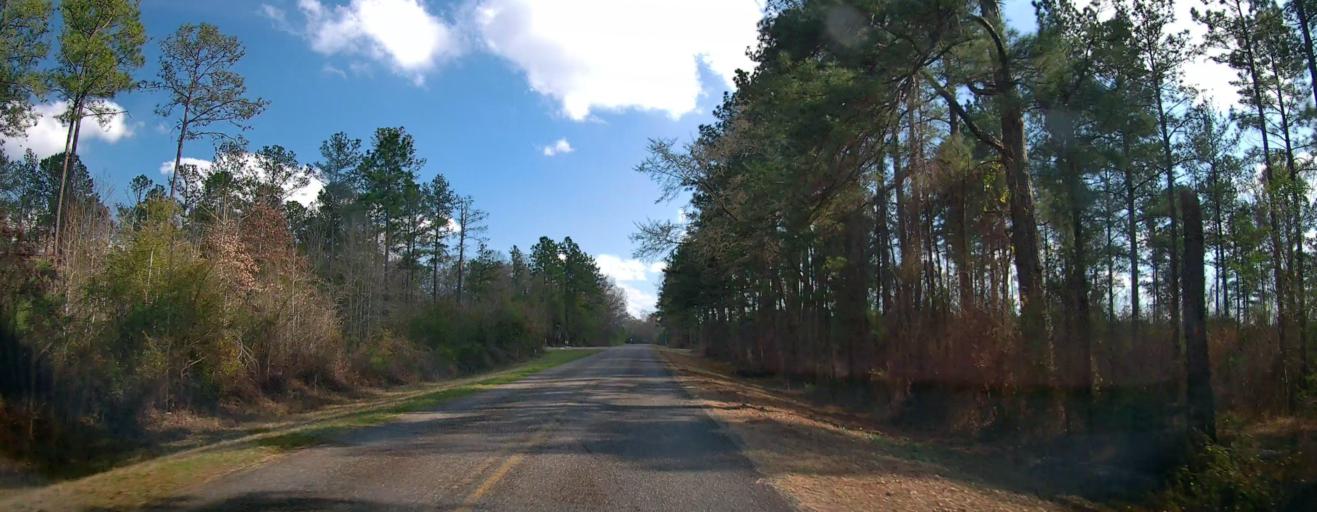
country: US
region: Georgia
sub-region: Twiggs County
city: Jeffersonville
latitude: 32.6701
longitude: -83.2355
